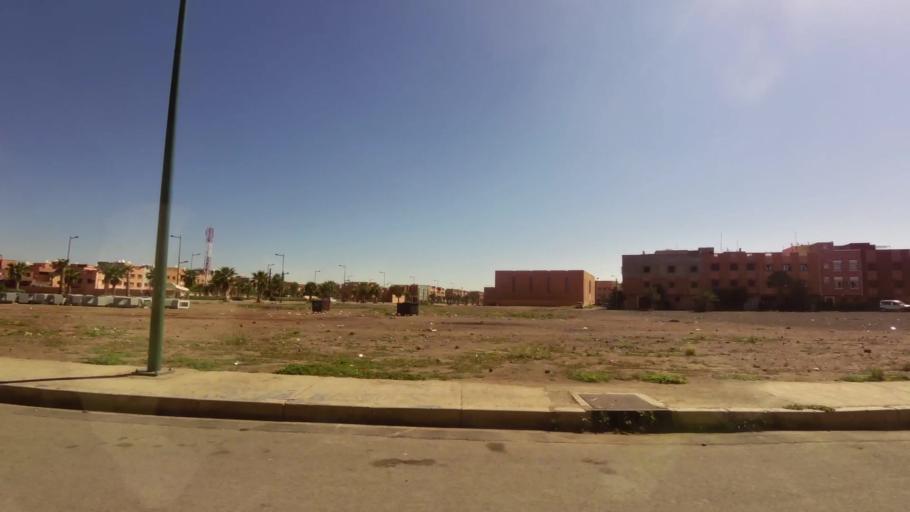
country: MA
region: Marrakech-Tensift-Al Haouz
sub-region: Marrakech
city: Marrakesh
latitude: 31.5889
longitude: -8.0554
